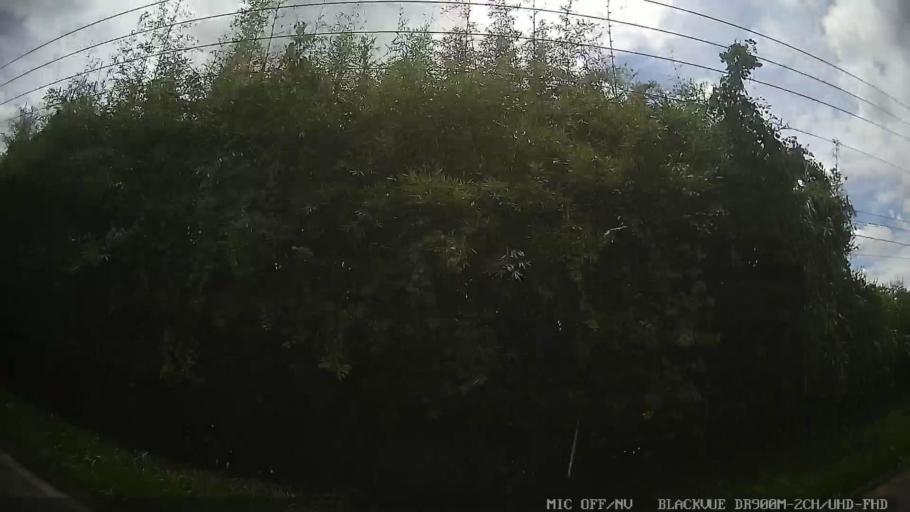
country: BR
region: Sao Paulo
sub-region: Suzano
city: Suzano
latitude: -23.5945
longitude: -46.3071
